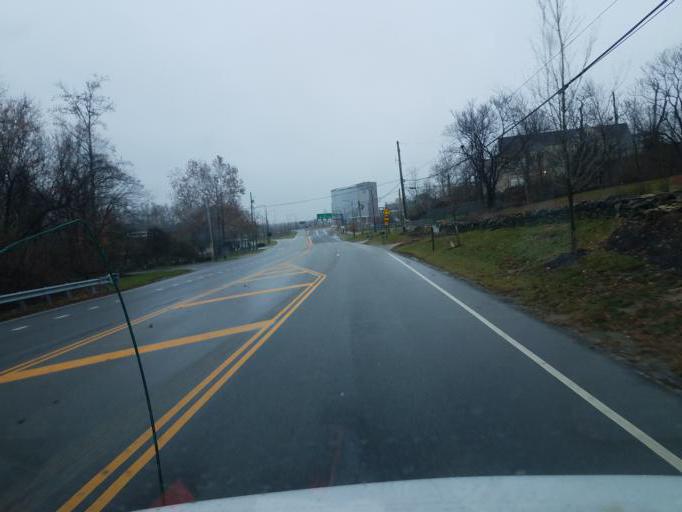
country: US
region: Ohio
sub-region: Franklin County
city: Dublin
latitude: 40.0967
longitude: -83.1084
